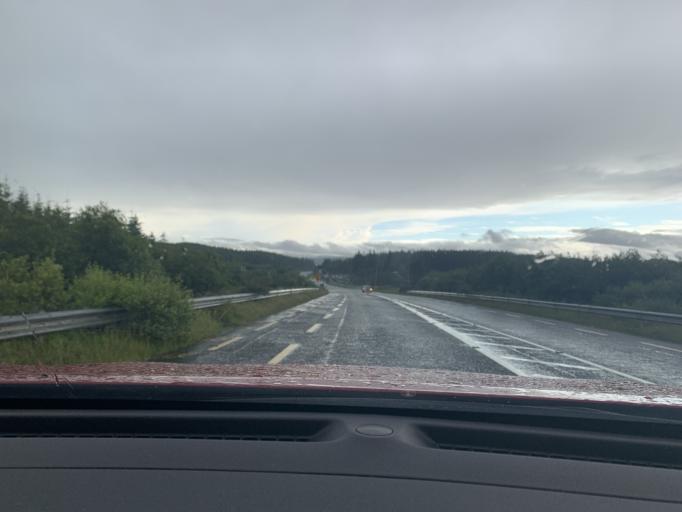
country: IE
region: Ulster
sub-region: County Donegal
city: Letterkenny
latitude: 54.8894
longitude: -7.7340
